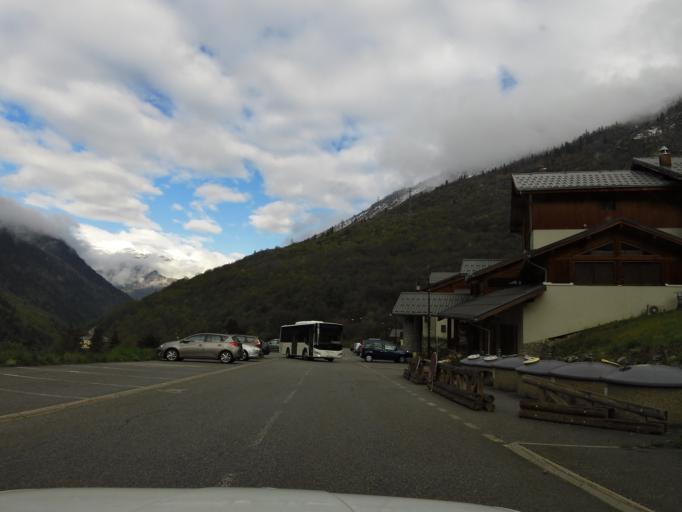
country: FR
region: Rhone-Alpes
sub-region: Departement de la Savoie
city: Saint-Michel-de-Maurienne
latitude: 45.2081
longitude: 6.5519
